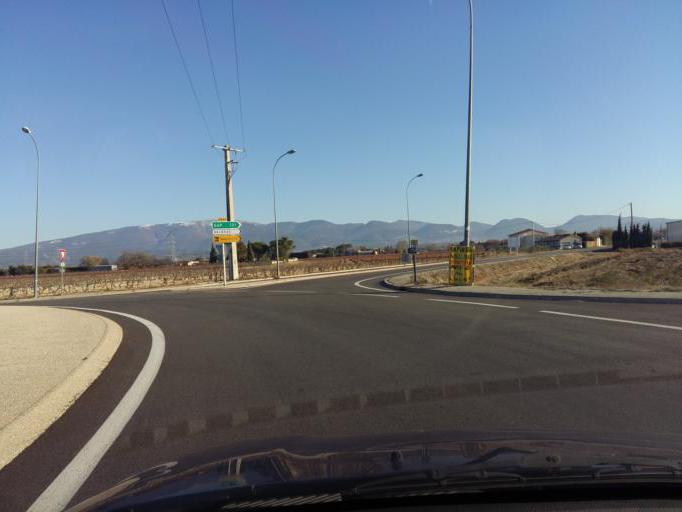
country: FR
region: Provence-Alpes-Cote d'Azur
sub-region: Departement du Vaucluse
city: Valreas
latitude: 44.3885
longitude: 4.9721
